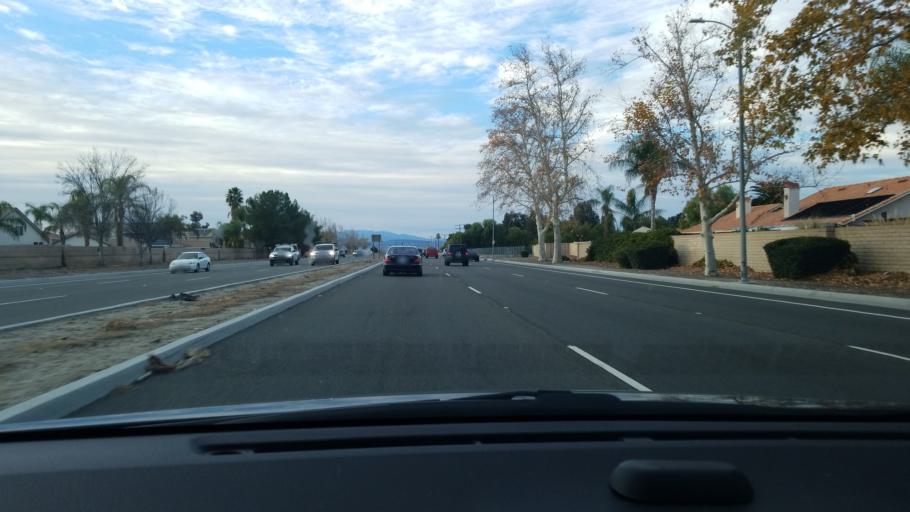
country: US
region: California
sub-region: Riverside County
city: San Jacinto
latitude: 33.8070
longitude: -116.9805
